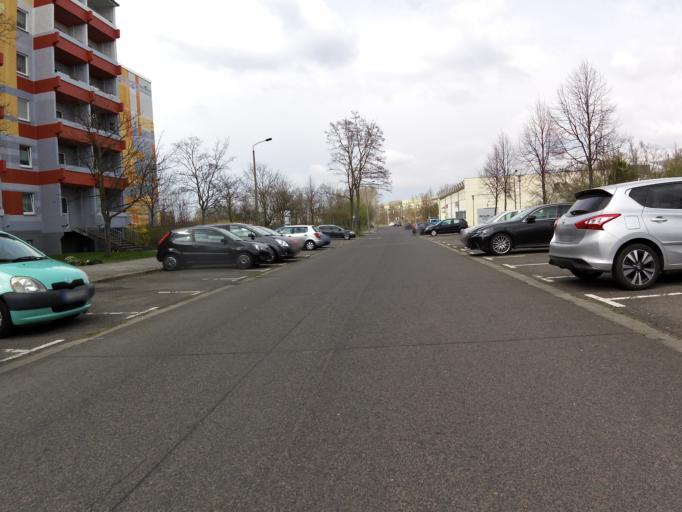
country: DE
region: Saxony
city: Markranstadt
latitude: 51.3204
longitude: 12.2870
